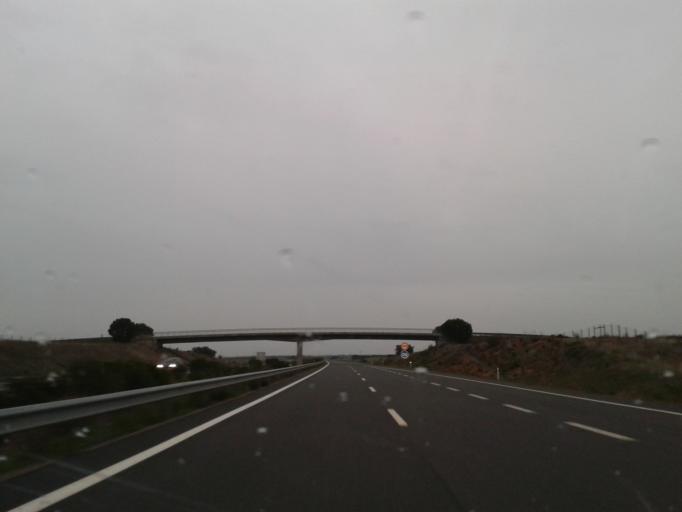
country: PT
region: Beja
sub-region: Aljustrel
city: Aljustrel
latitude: 37.9282
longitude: -8.2424
